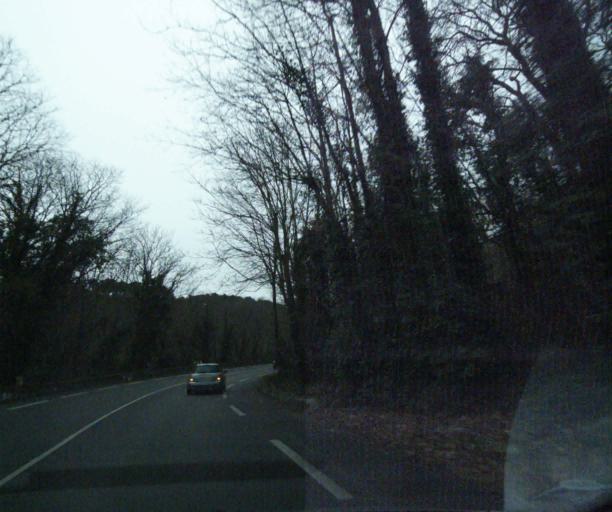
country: FR
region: Provence-Alpes-Cote d'Azur
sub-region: Departement des Bouches-du-Rhone
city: Aix-en-Provence
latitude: 43.5517
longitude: 5.4624
